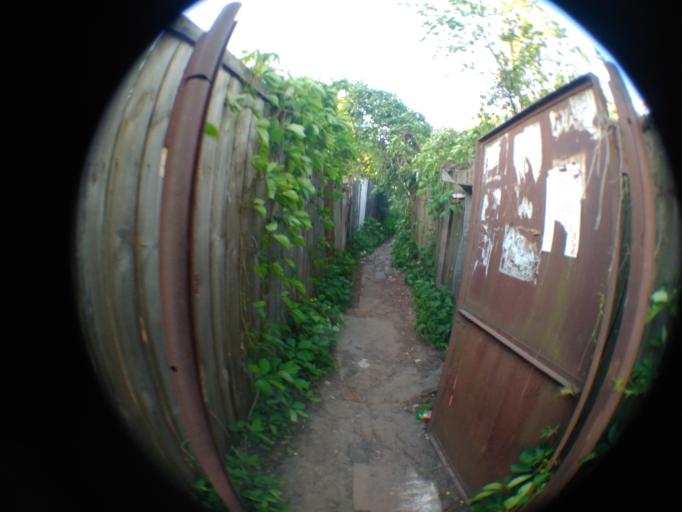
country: RU
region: Moskovskaya
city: Zhukovskiy
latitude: 55.5826
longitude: 38.1013
